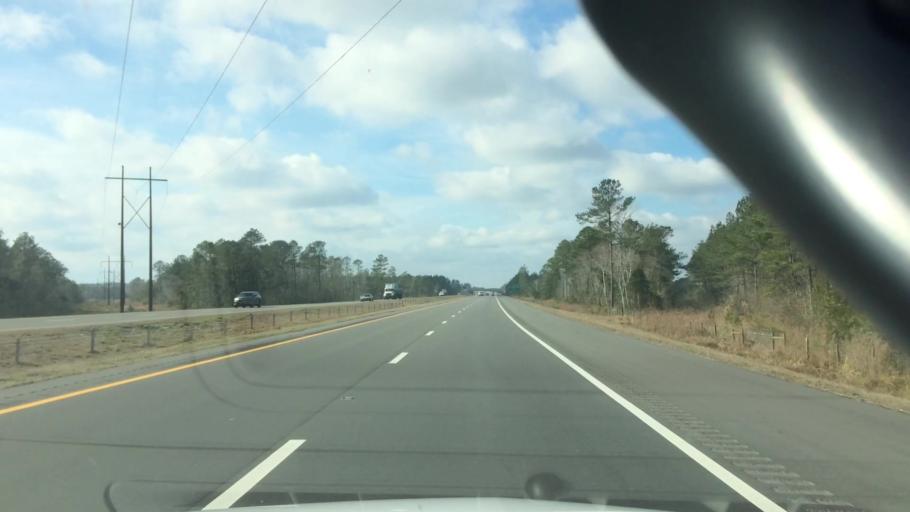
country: US
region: North Carolina
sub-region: Brunswick County
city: Leland
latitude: 34.2742
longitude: -78.0347
